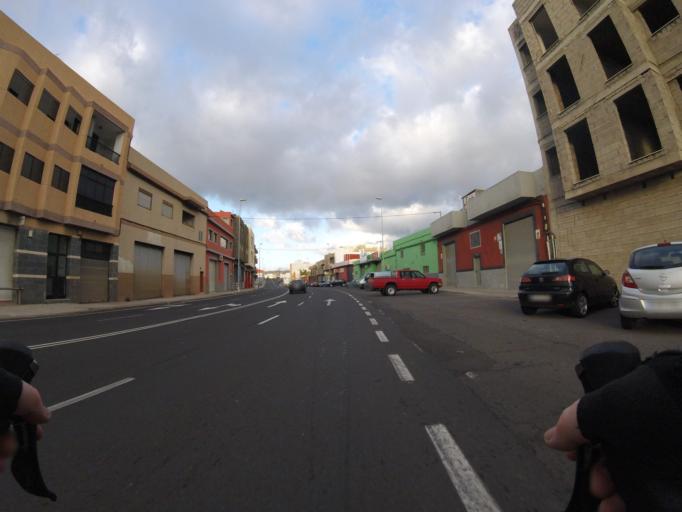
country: ES
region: Canary Islands
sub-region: Provincia de Santa Cruz de Tenerife
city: La Laguna
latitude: 28.4248
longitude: -16.3174
